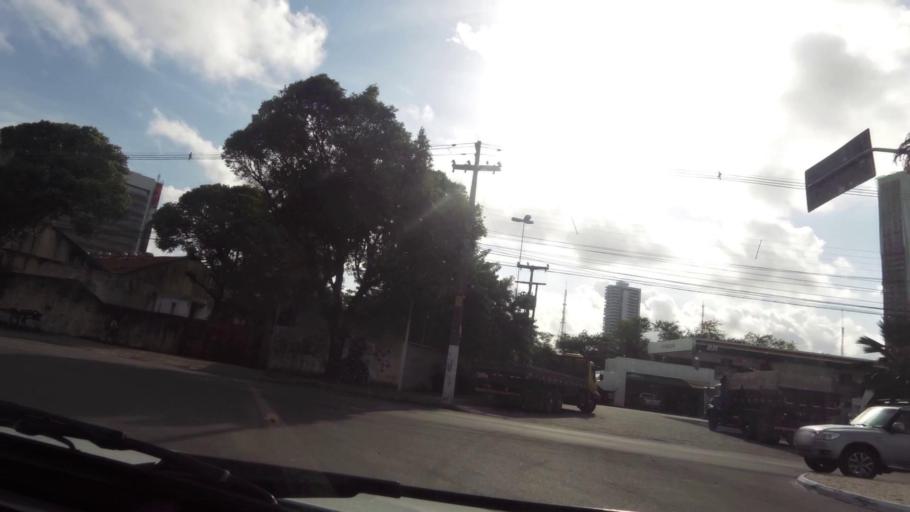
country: BR
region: Pernambuco
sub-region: Recife
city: Recife
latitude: -8.0525
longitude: -34.8718
